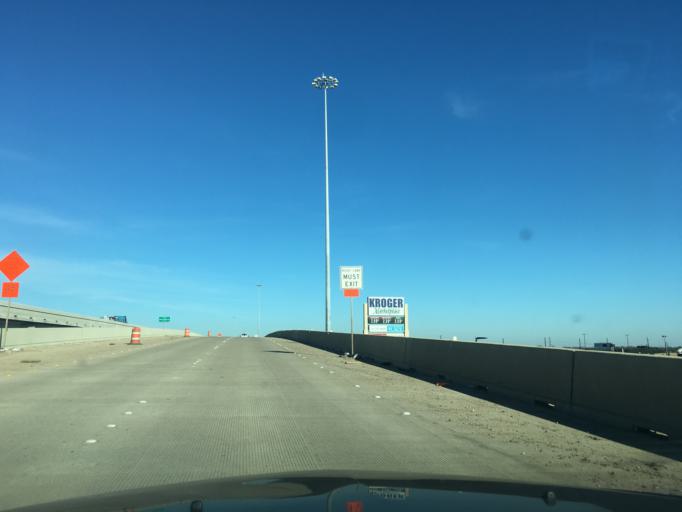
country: US
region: Texas
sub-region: Fort Bend County
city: Richmond
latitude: 29.5456
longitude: -95.7481
